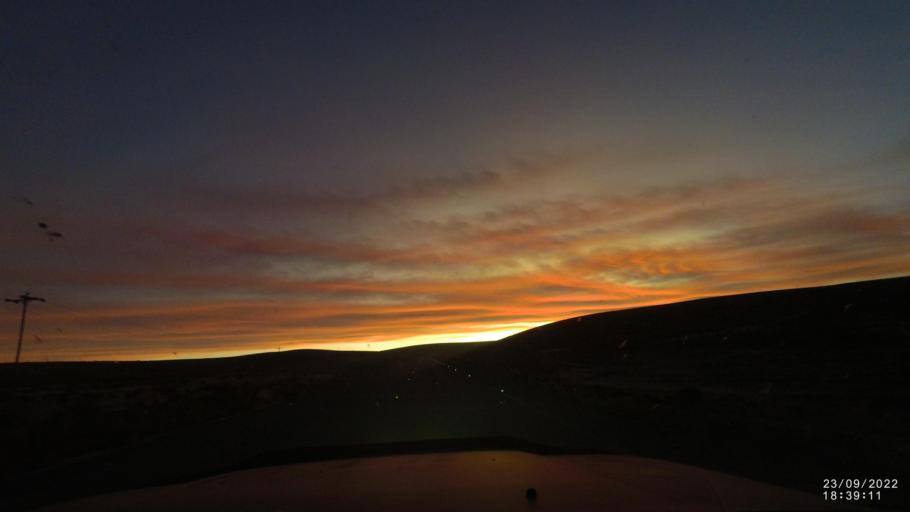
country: BO
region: Oruro
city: Challapata
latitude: -19.4177
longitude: -67.3247
